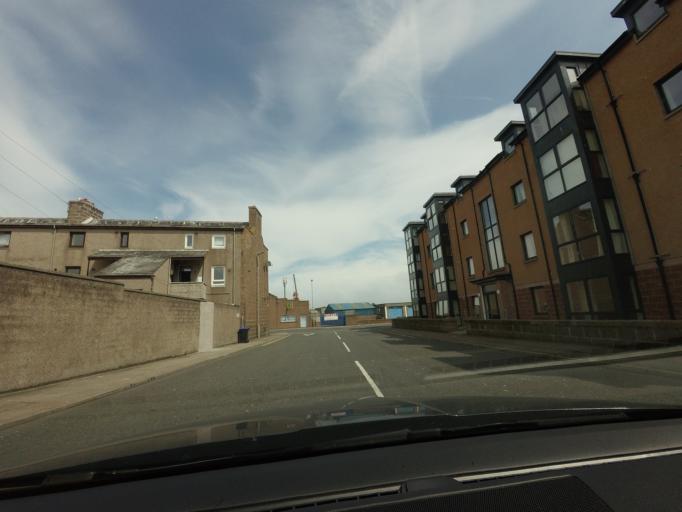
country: GB
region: Scotland
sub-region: Aberdeenshire
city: Peterhead
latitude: 57.5096
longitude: -1.7811
